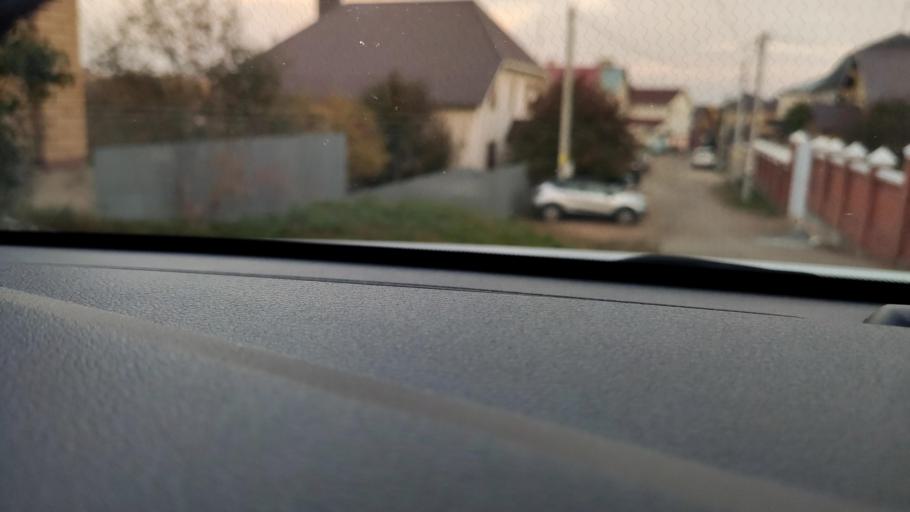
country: RU
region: Tatarstan
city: Stolbishchi
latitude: 55.7569
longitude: 49.2508
